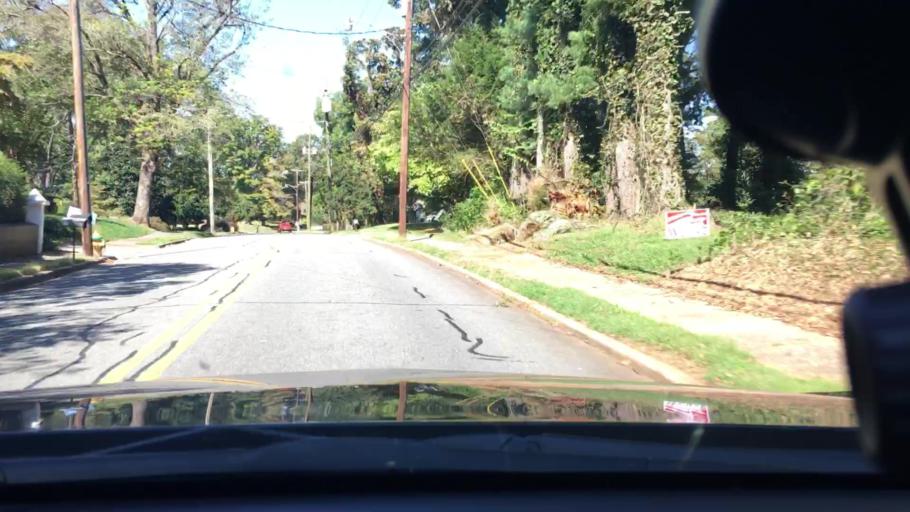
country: US
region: North Carolina
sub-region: Rutherford County
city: Rutherfordton
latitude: 35.3761
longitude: -81.9605
